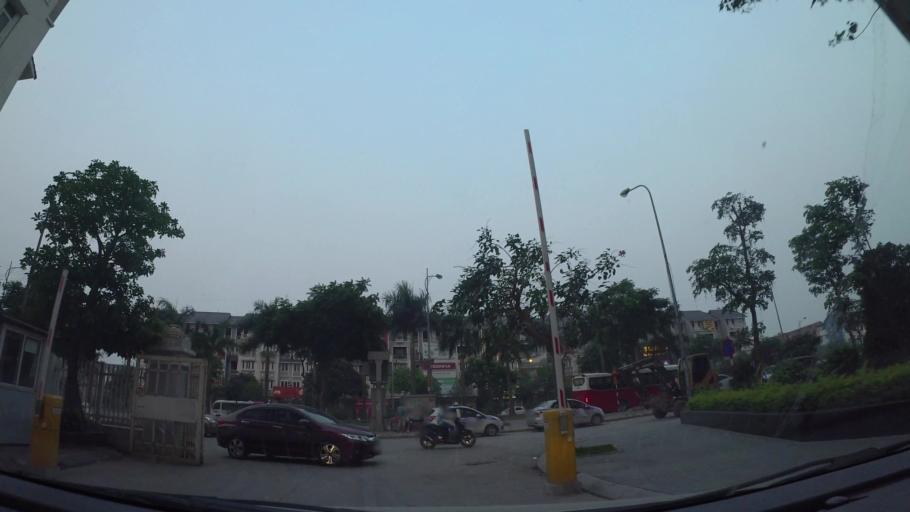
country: VN
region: Ha Noi
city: Cau Dien
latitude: 21.0034
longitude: 105.7323
